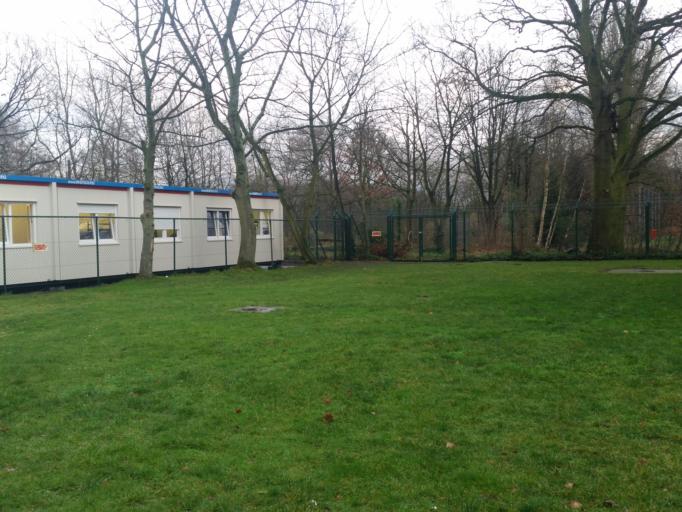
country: BE
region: Flanders
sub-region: Provincie Antwerpen
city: Kapellen
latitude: 51.3095
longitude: 4.4557
